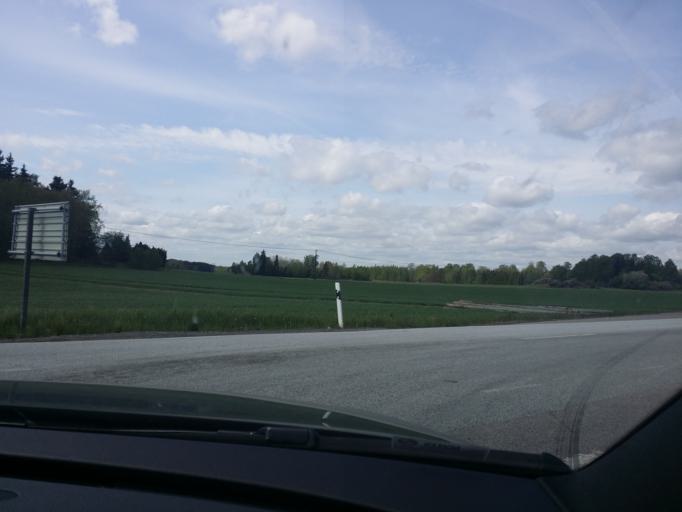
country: SE
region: Uppsala
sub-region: Habo Kommun
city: Balsta
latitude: 59.6312
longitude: 17.5986
